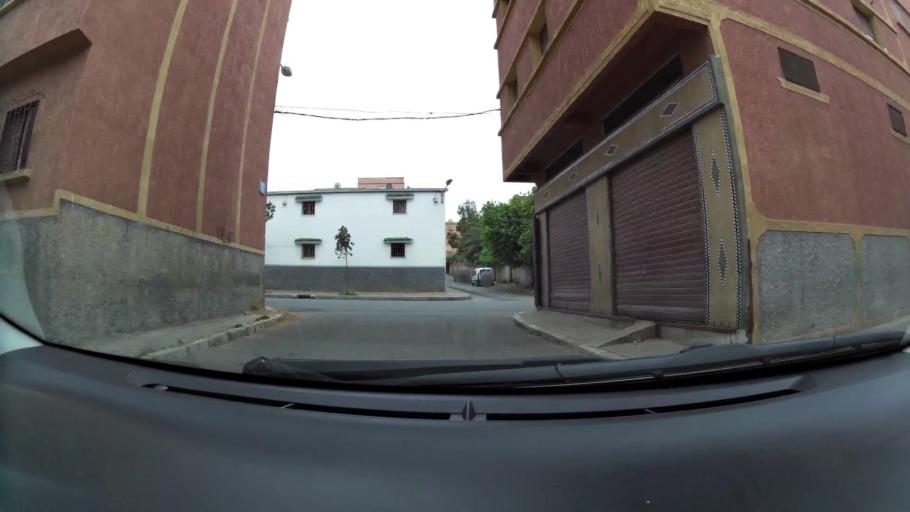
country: MA
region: Grand Casablanca
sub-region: Casablanca
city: Casablanca
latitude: 33.5667
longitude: -7.5613
